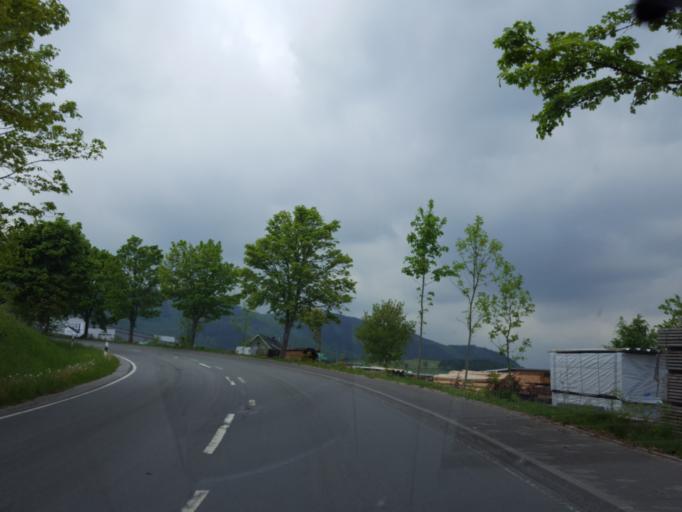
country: DE
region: North Rhine-Westphalia
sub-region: Regierungsbezirk Arnsberg
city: Olsberg
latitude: 51.3088
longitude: 8.5021
